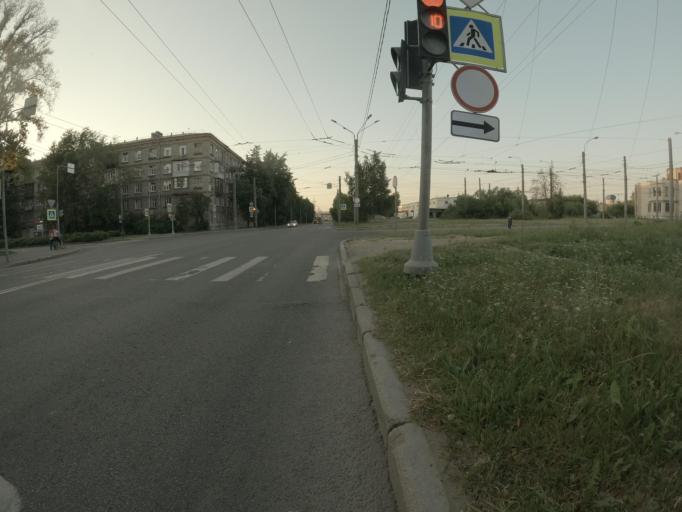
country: RU
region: St.-Petersburg
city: Avtovo
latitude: 59.8762
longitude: 30.2774
